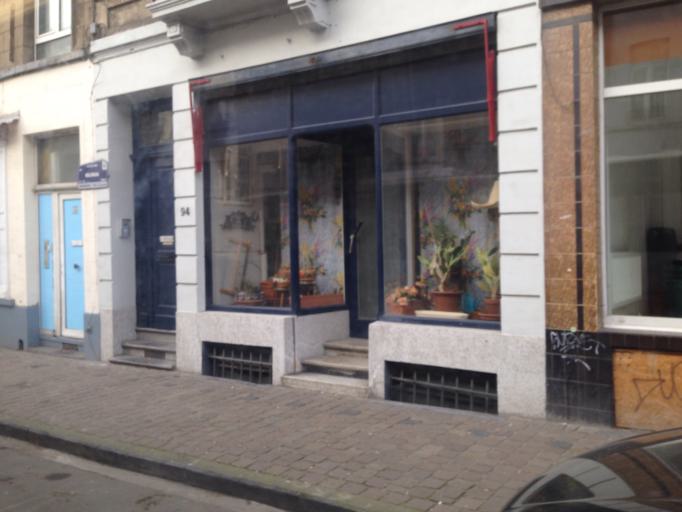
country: BE
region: Brussels Capital
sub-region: Bruxelles-Capitale
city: Brussels
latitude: 50.8317
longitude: 4.3741
